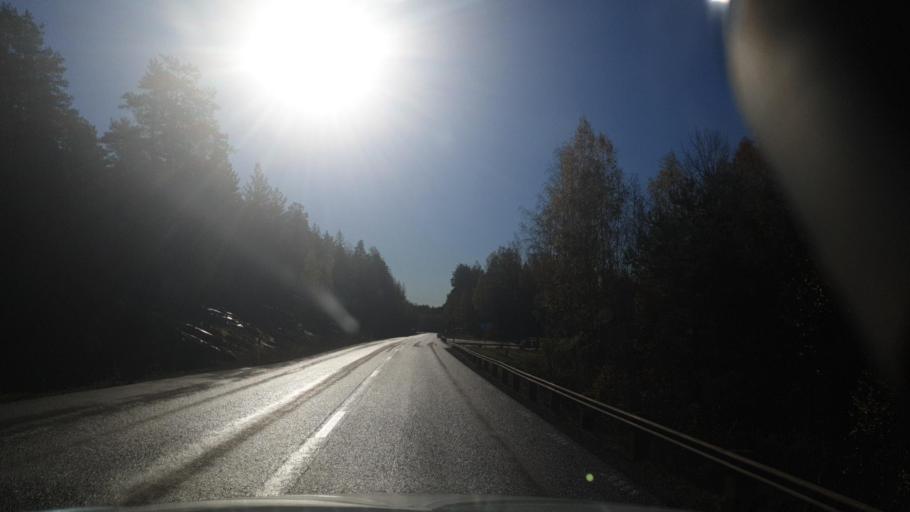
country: SE
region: Vaermland
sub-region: Arvika Kommun
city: Arvika
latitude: 59.5621
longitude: 12.7234
